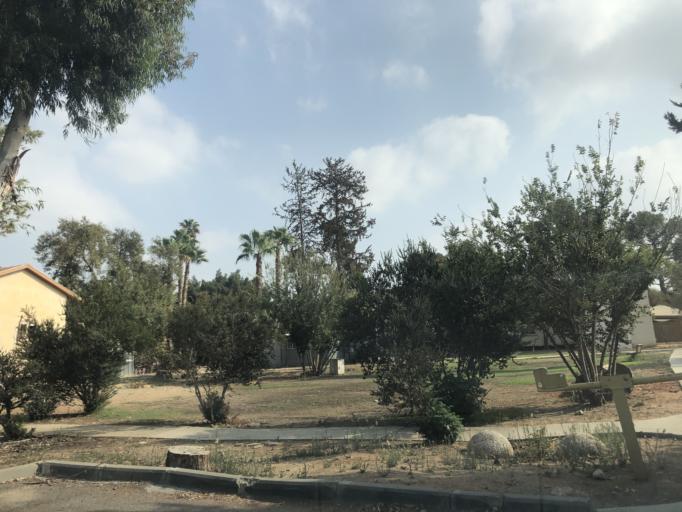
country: IL
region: Central District
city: Rosh Ha'Ayin
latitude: 32.0840
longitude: 34.9382
